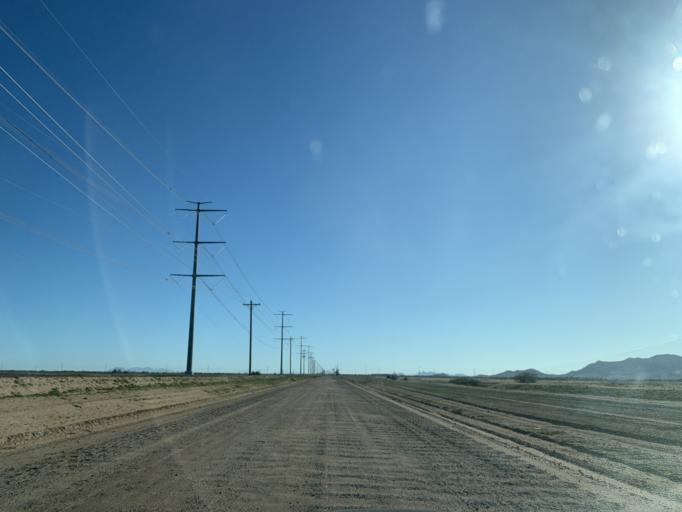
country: US
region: Arizona
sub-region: Pinal County
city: Casa Grande
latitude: 32.8588
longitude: -111.6710
